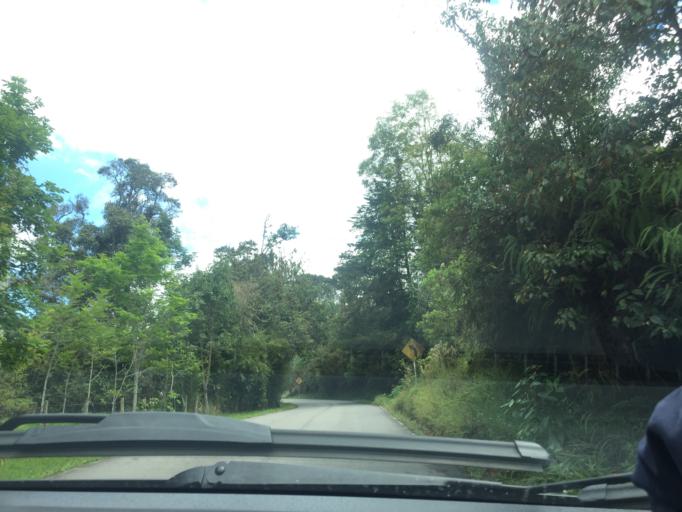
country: CO
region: Cundinamarca
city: Supata
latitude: 5.0524
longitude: -74.2466
